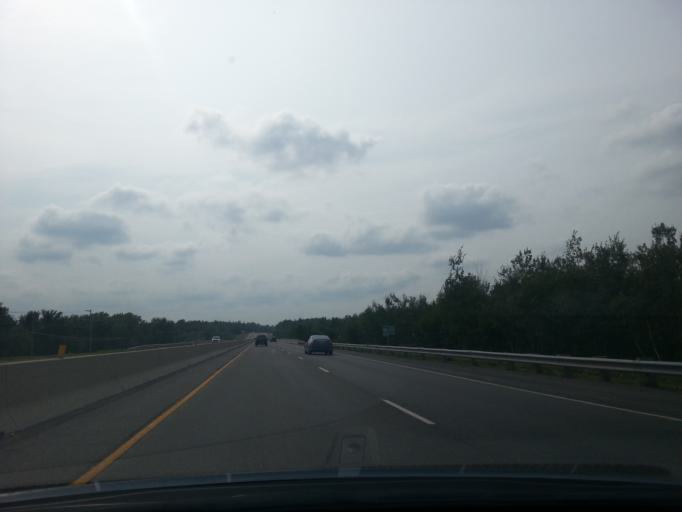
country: CA
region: New Brunswick
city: Oromocto
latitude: 45.8437
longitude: -66.5163
